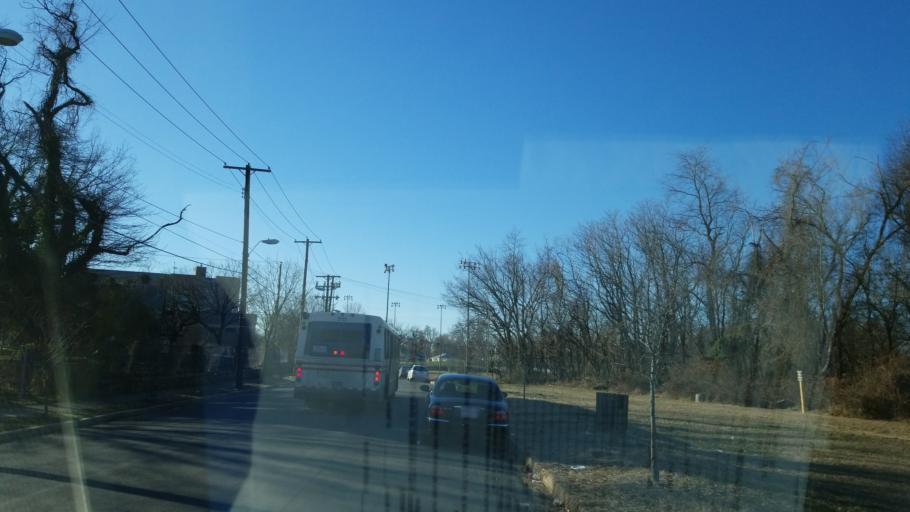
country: US
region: Maryland
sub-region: Prince George's County
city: Glassmanor
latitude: 38.8295
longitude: -77.0137
